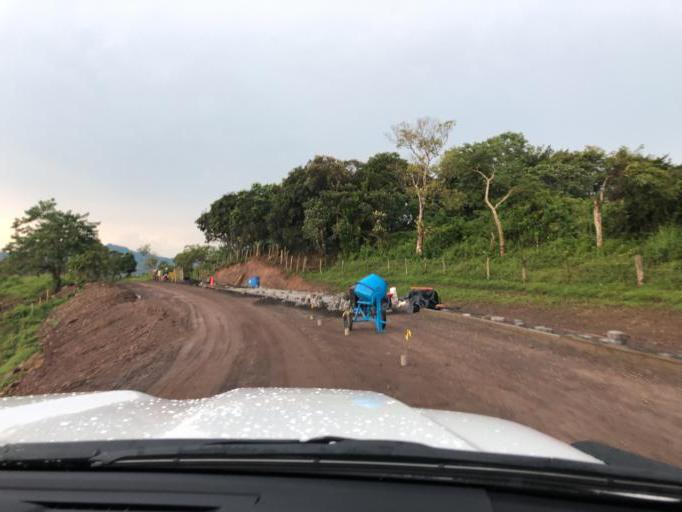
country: NI
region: Chontales
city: La Libertad
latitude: 12.2042
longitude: -85.1736
